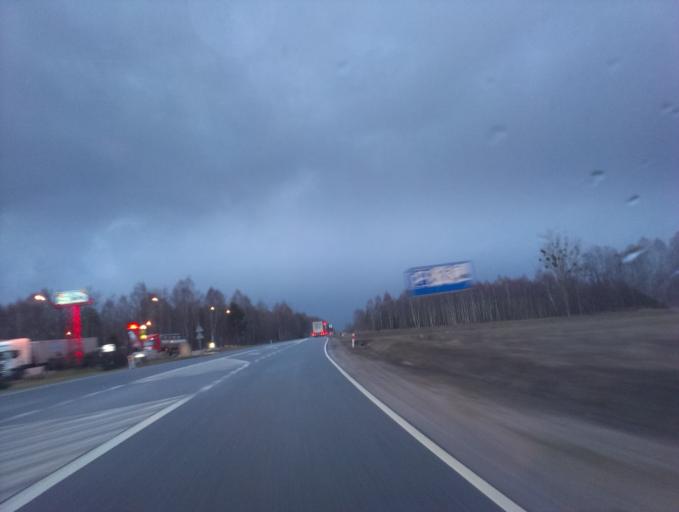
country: PL
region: Lodz Voivodeship
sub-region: Powiat opoczynski
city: Zarnow
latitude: 51.2293
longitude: 20.1780
